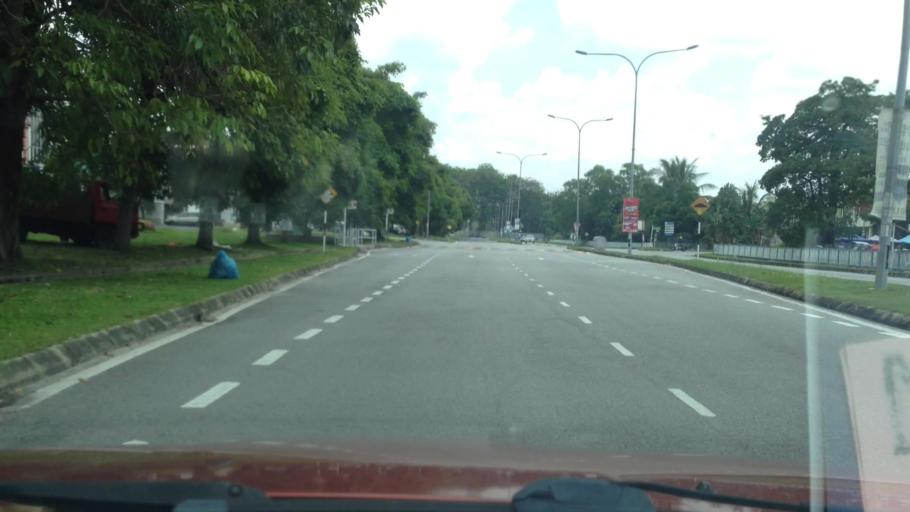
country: MY
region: Selangor
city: Kampung Baru Subang
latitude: 3.1657
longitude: 101.5484
